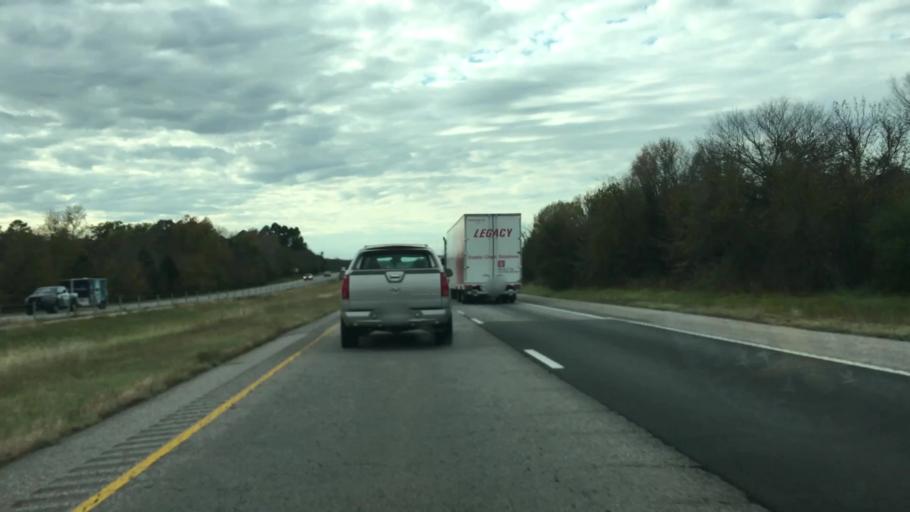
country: US
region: Arkansas
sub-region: Conway County
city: Morrilton
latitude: 35.1633
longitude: -92.6311
